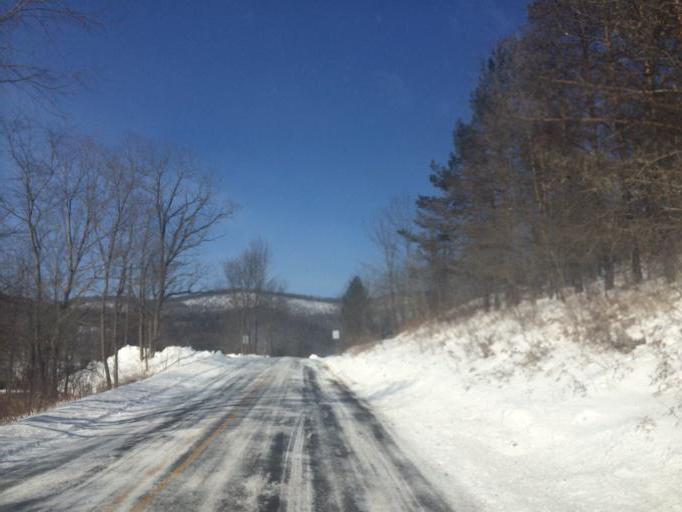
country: US
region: Pennsylvania
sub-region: Centre County
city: Stormstown
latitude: 40.8569
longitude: -78.0210
